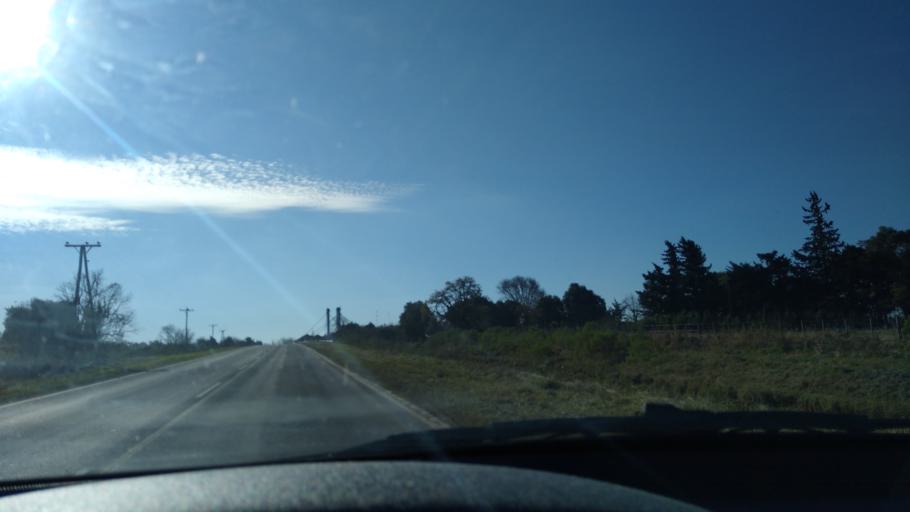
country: AR
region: Entre Rios
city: Aranguren
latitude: -32.3663
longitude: -60.3447
